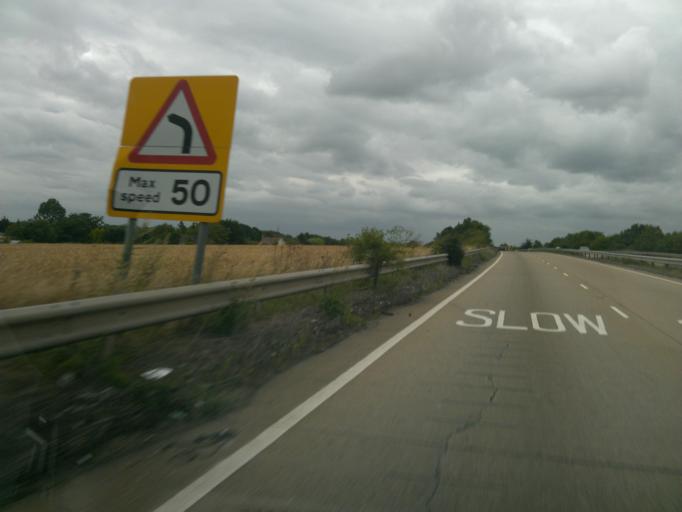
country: GB
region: England
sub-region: Essex
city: Great Bentley
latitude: 51.8808
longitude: 1.0484
